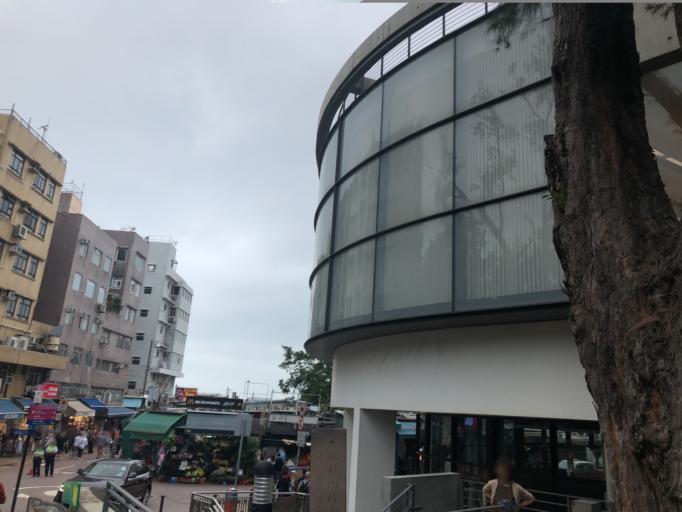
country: HK
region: Wanchai
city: Wan Chai
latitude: 22.2191
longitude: 114.2127
